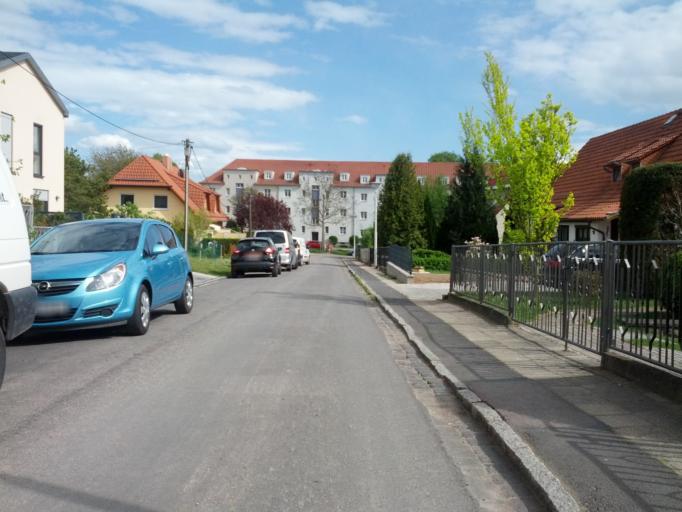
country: DE
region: Thuringia
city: Eisenach
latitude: 50.9882
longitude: 10.3072
